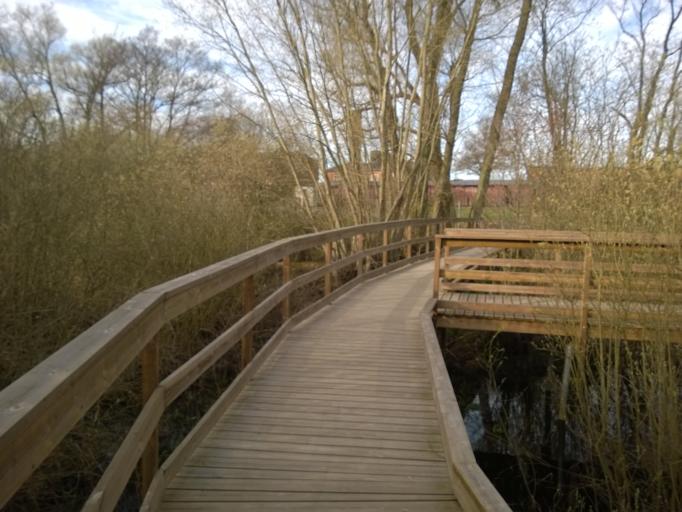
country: SE
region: Skane
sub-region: Kristianstads Kommun
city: Kristianstad
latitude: 56.0331
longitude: 14.1467
